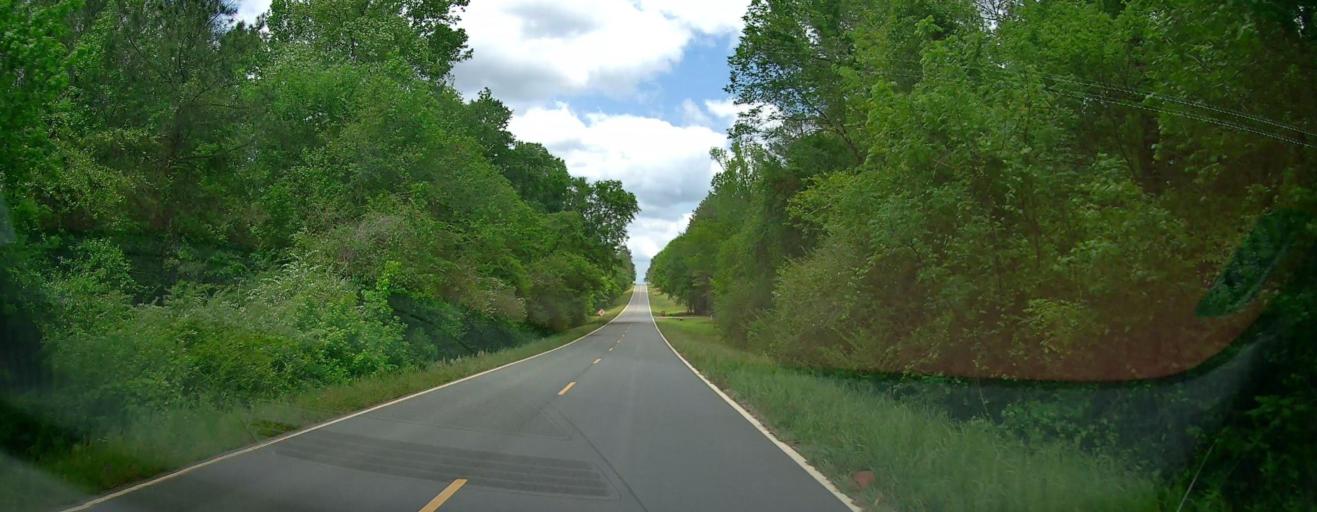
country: US
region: Georgia
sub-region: Laurens County
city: Dublin
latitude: 32.6249
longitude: -82.9761
